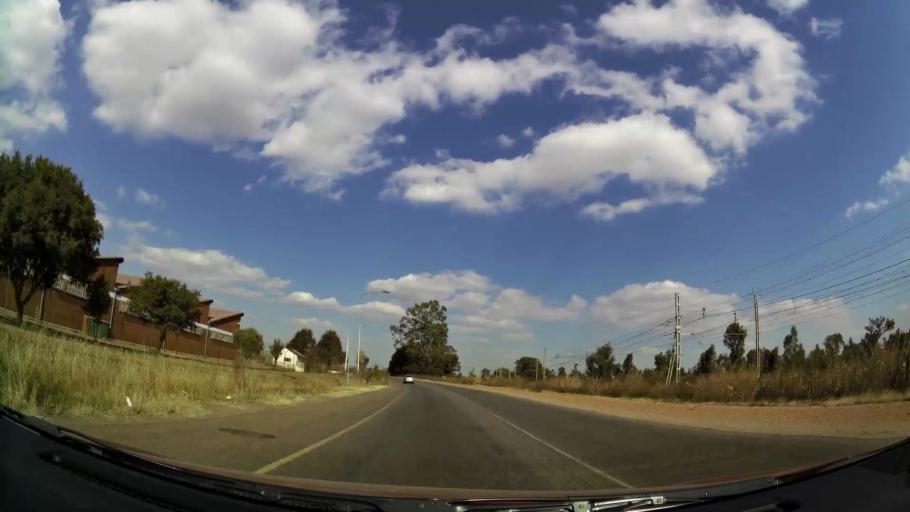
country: ZA
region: Gauteng
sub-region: Ekurhuleni Metropolitan Municipality
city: Tembisa
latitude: -25.9811
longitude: 28.2450
